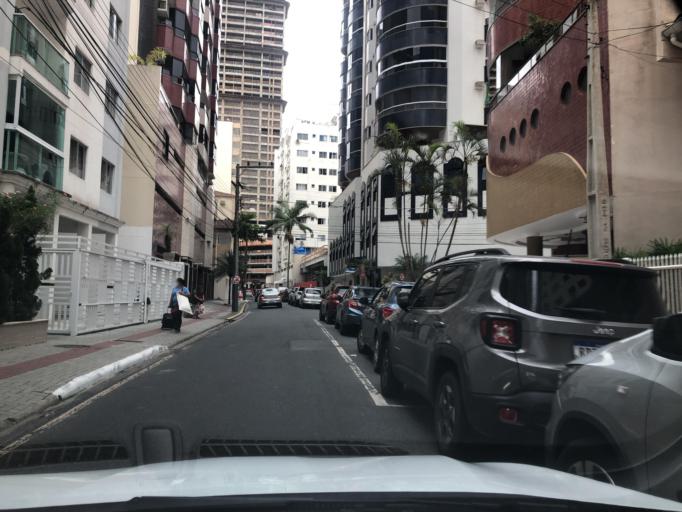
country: BR
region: Santa Catarina
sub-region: Balneario Camboriu
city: Balneario Camboriu
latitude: -27.0000
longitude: -48.6231
